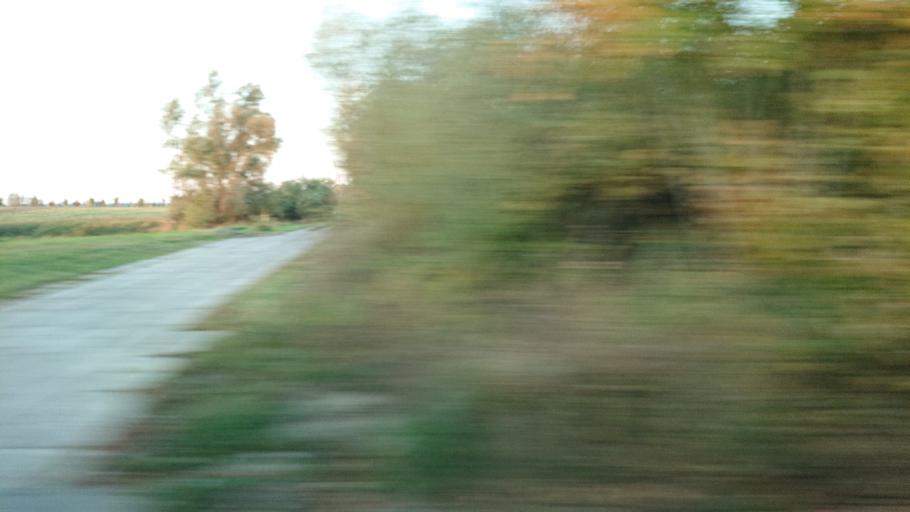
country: DE
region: Mecklenburg-Vorpommern
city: Greifswald
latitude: 54.0637
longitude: 13.3794
